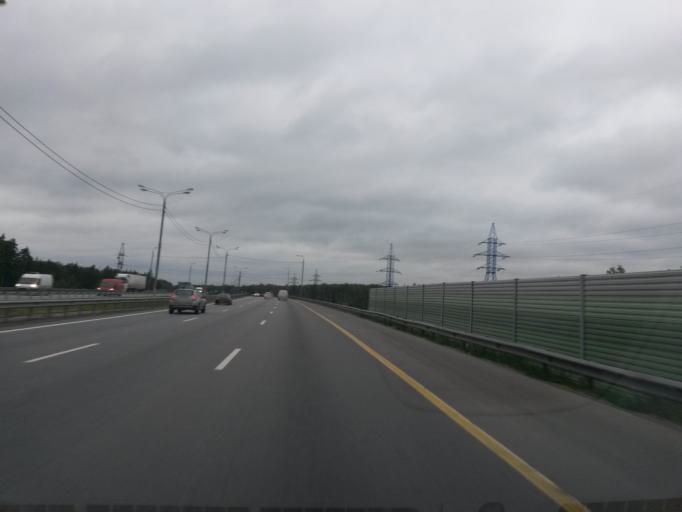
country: RU
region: Moskovskaya
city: Vostryakovo
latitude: 55.4141
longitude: 37.7940
